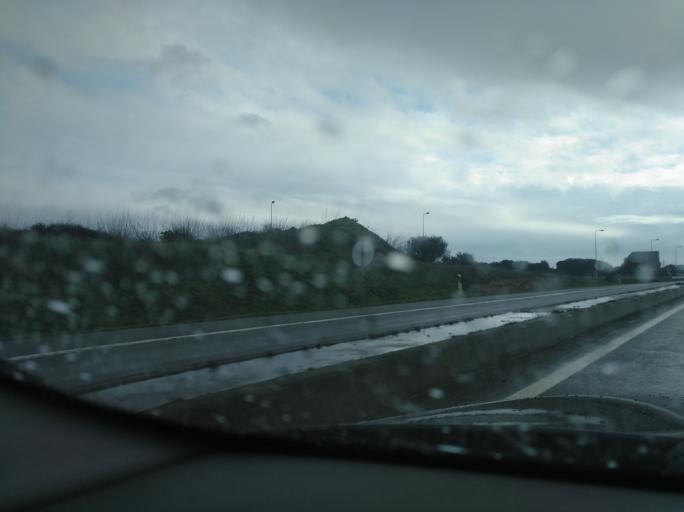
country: PT
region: Setubal
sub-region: Grandola
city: Grandola
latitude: 38.1123
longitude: -8.4182
